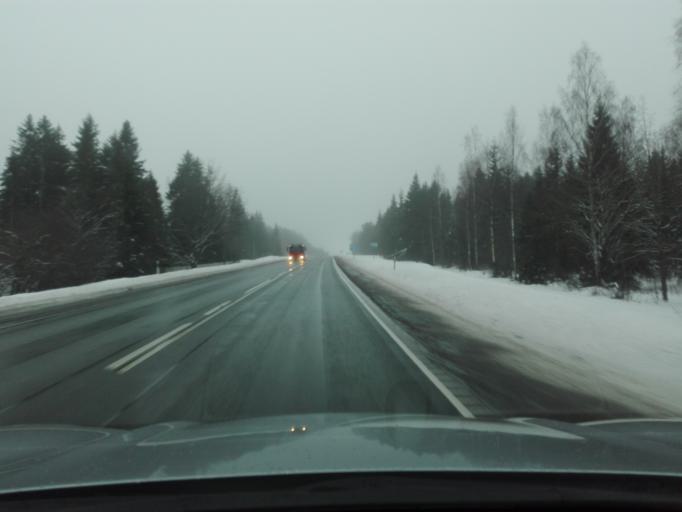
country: EE
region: Raplamaa
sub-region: Kohila vald
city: Kohila
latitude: 59.1862
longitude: 24.7858
